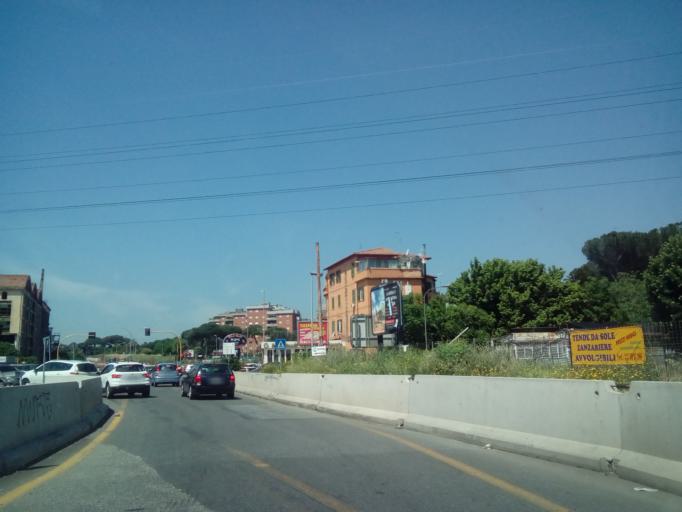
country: IT
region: Latium
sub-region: Citta metropolitana di Roma Capitale
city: Colle Verde
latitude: 41.9327
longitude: 12.5860
